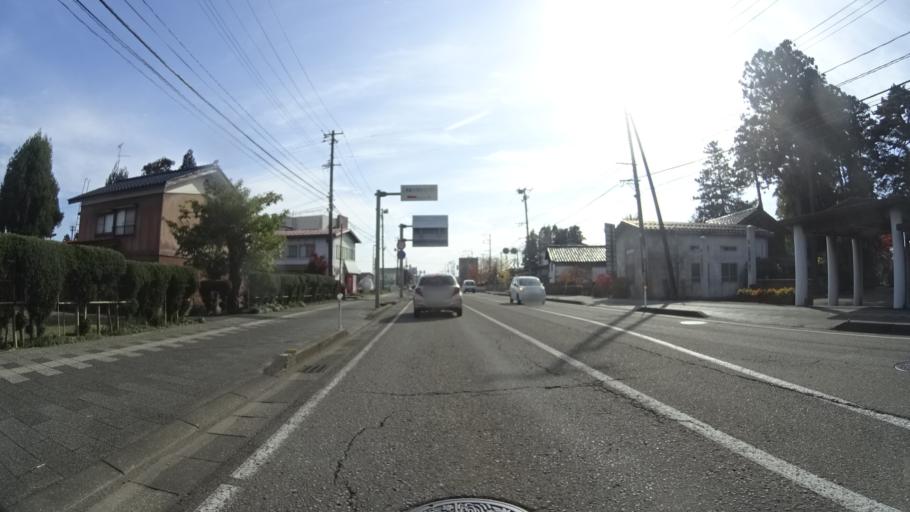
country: JP
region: Niigata
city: Joetsu
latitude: 37.1426
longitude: 138.2403
